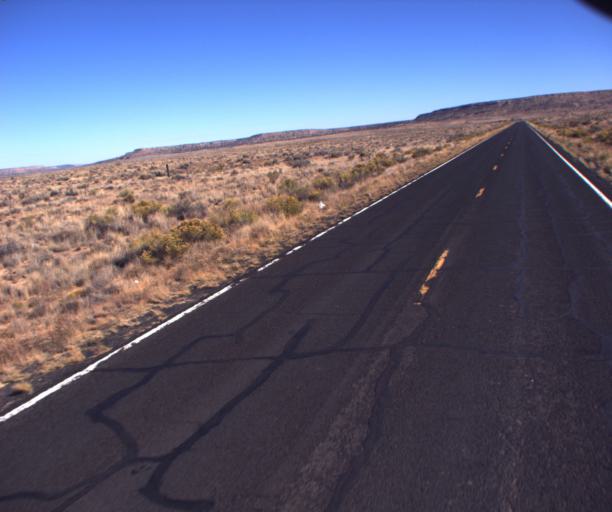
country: US
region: Arizona
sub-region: Navajo County
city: First Mesa
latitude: 35.8410
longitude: -110.3395
